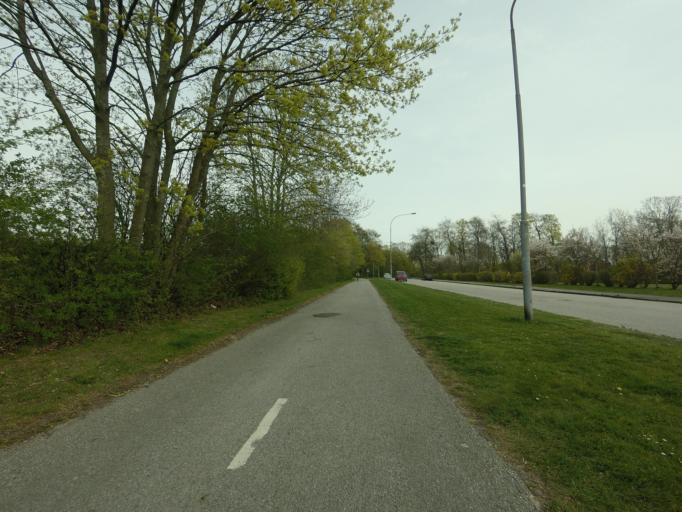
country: SE
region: Skane
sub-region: Lunds Kommun
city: Lund
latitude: 55.7217
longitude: 13.1690
